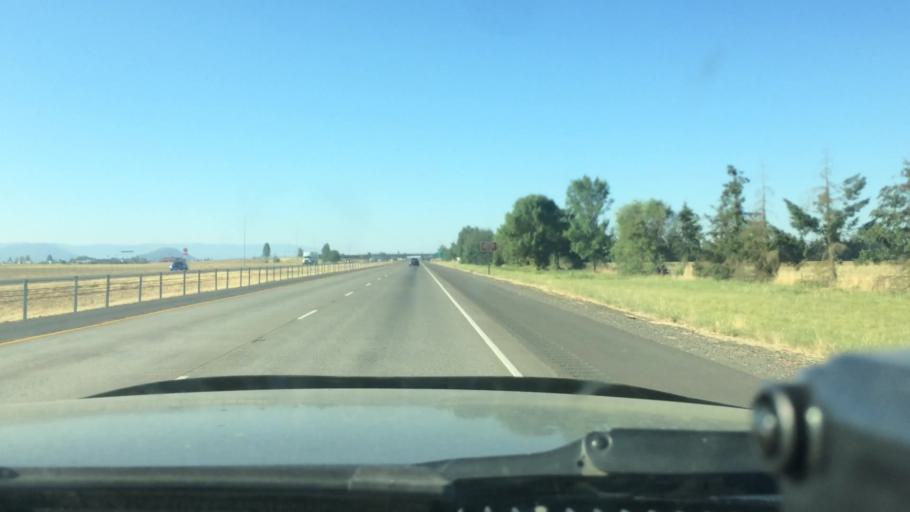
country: US
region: Oregon
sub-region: Linn County
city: Tangent
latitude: 44.5653
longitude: -123.0621
